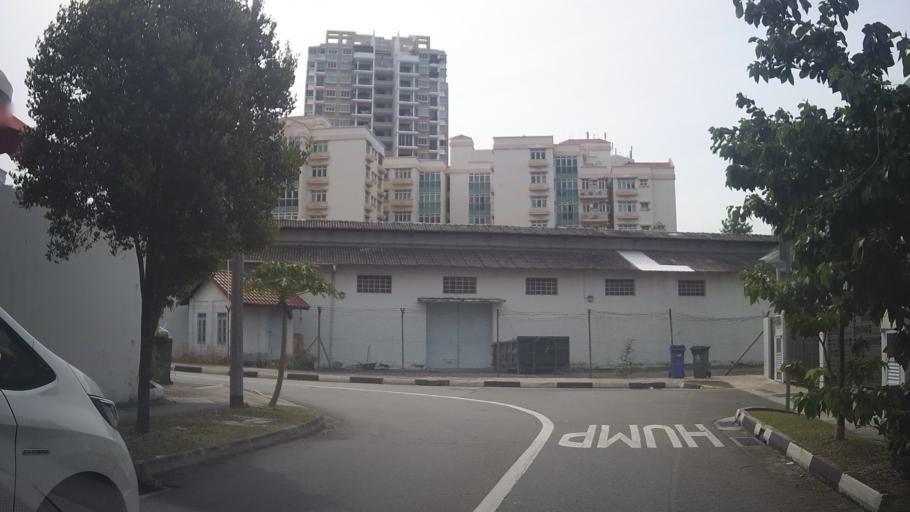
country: SG
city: Singapore
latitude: 1.3281
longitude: 103.8650
